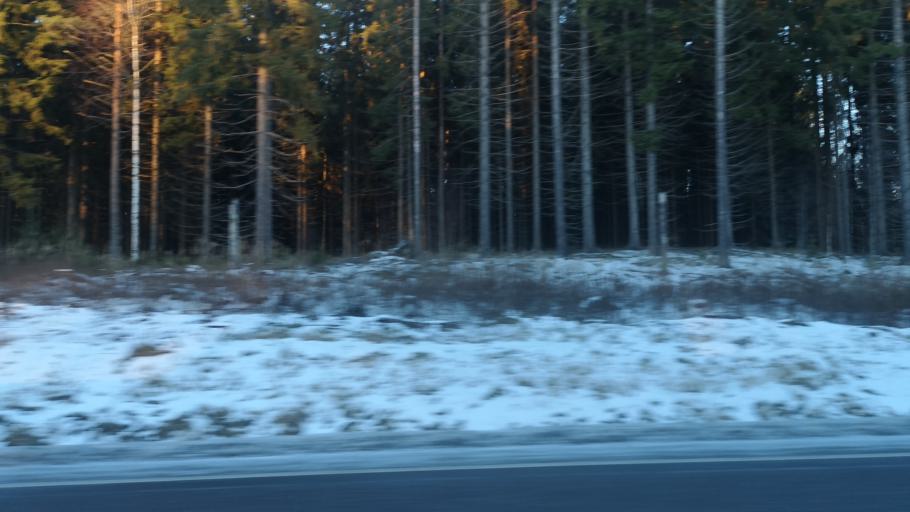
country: FI
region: Southern Savonia
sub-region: Savonlinna
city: Rantasalmi
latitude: 61.9559
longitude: 28.4020
